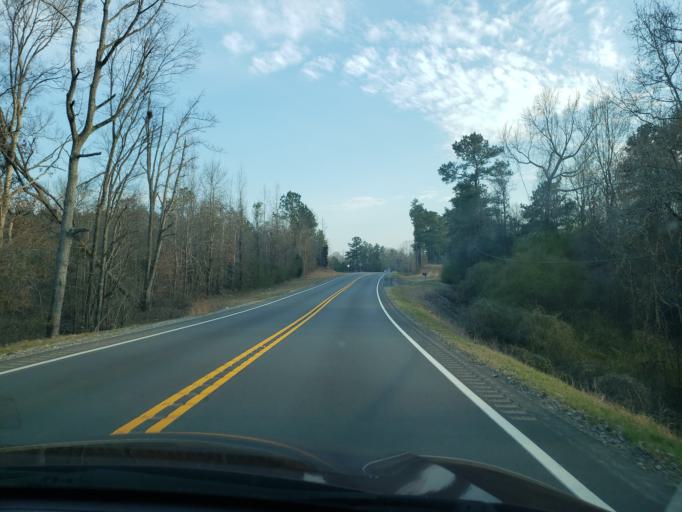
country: US
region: Alabama
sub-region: Hale County
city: Moundville
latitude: 32.8850
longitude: -87.6085
